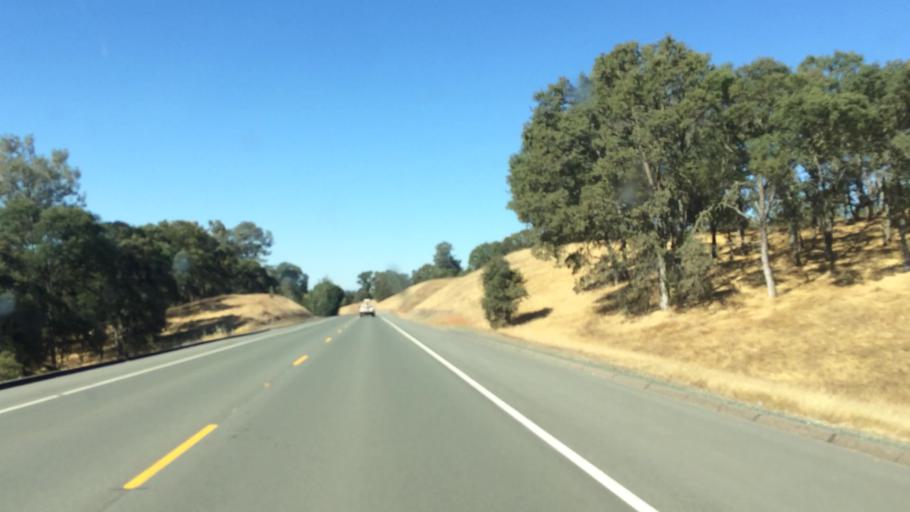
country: US
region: California
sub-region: Amador County
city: Plymouth
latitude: 38.4420
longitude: -120.8748
